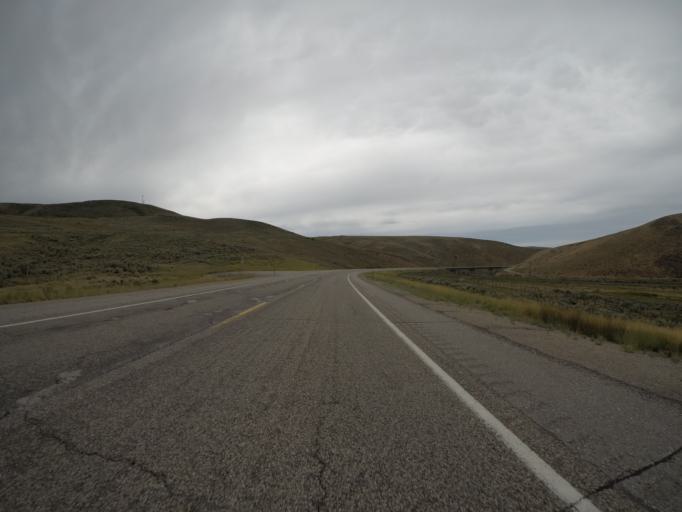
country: US
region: Wyoming
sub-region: Lincoln County
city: Kemmerer
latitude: 41.8176
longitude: -110.8030
